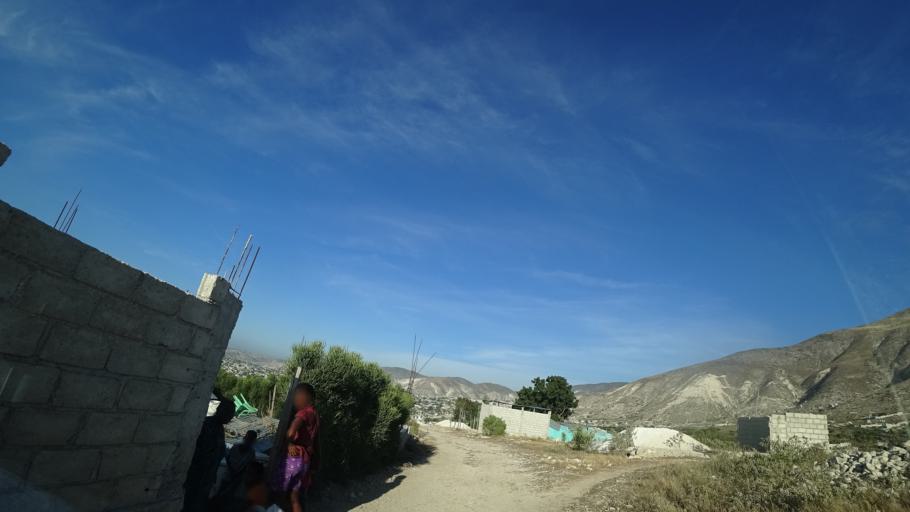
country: HT
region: Ouest
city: Croix des Bouquets
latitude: 18.6695
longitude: -72.2261
